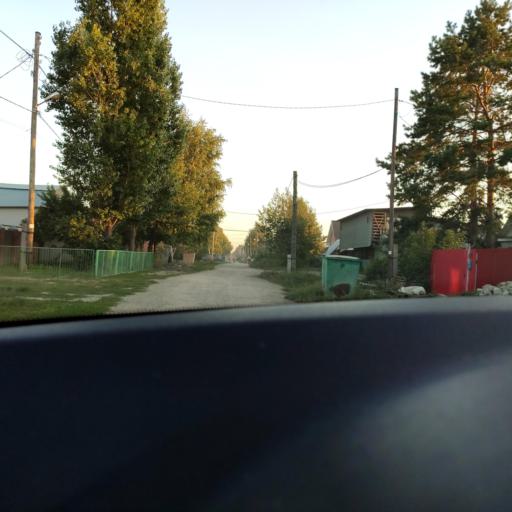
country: RU
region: Samara
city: Petra-Dubrava
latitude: 53.2586
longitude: 50.3247
